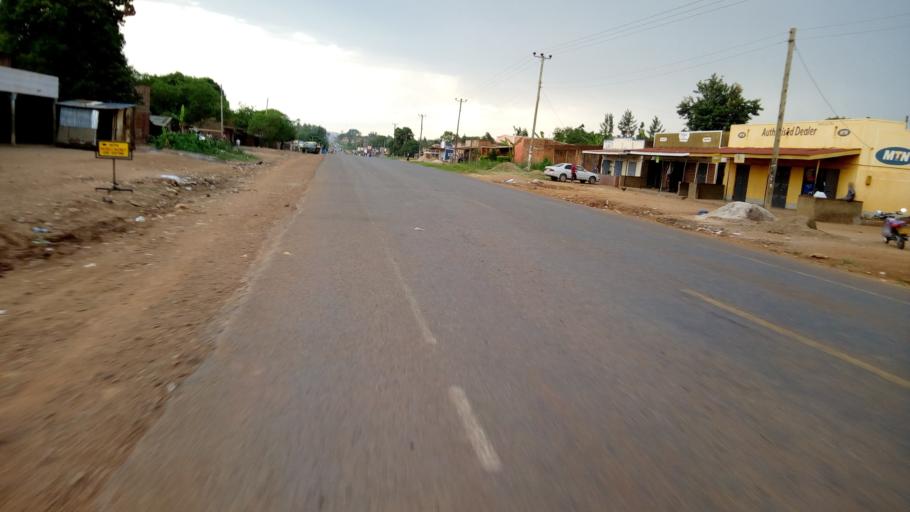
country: UG
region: Eastern Region
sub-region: Mbale District
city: Mbale
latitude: 1.1159
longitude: 34.1707
